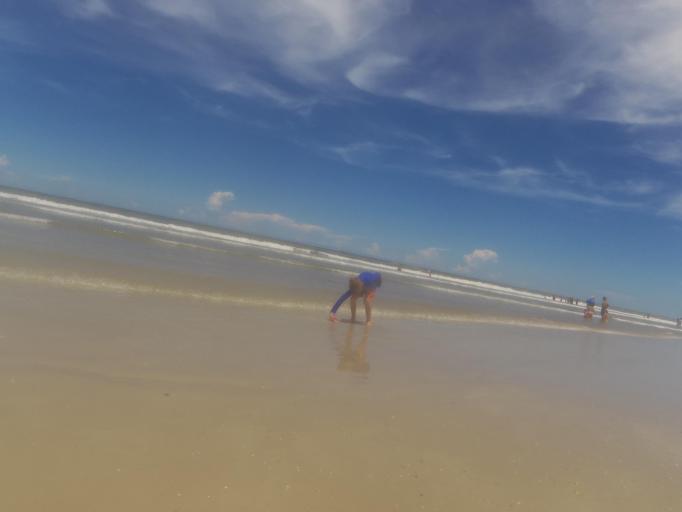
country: US
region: Florida
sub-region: Saint Johns County
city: Butler Beach
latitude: 29.8237
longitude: -81.2623
